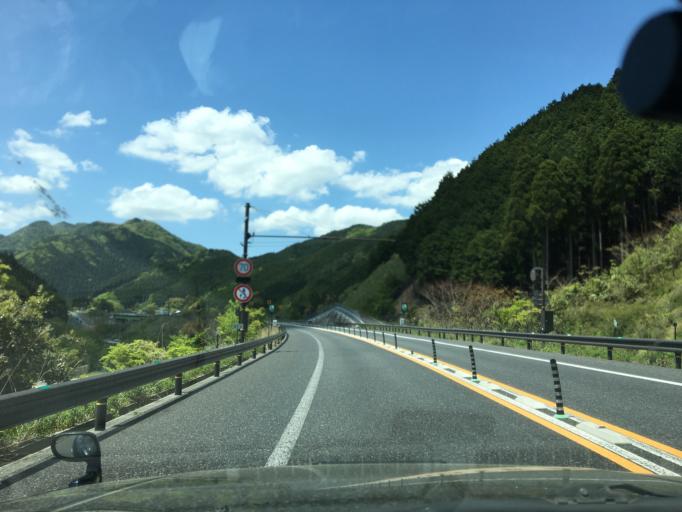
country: JP
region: Kyoto
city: Fukuchiyama
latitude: 35.2904
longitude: 134.9738
